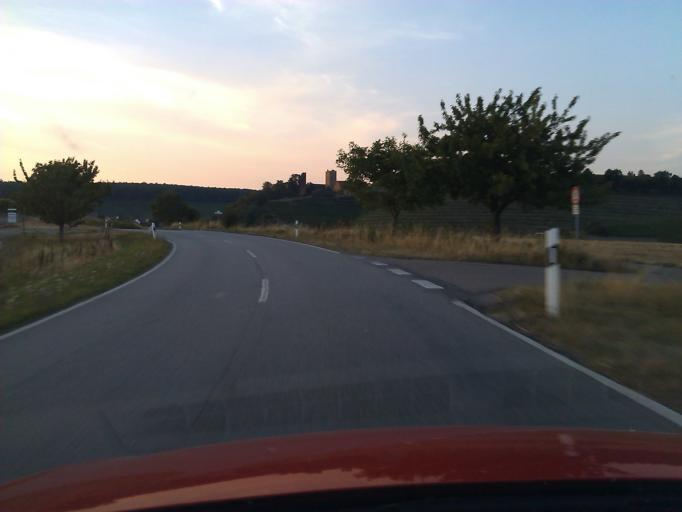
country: DE
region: Baden-Wuerttemberg
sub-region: Regierungsbezirk Stuttgart
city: Brackenheim
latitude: 49.0975
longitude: 9.0508
